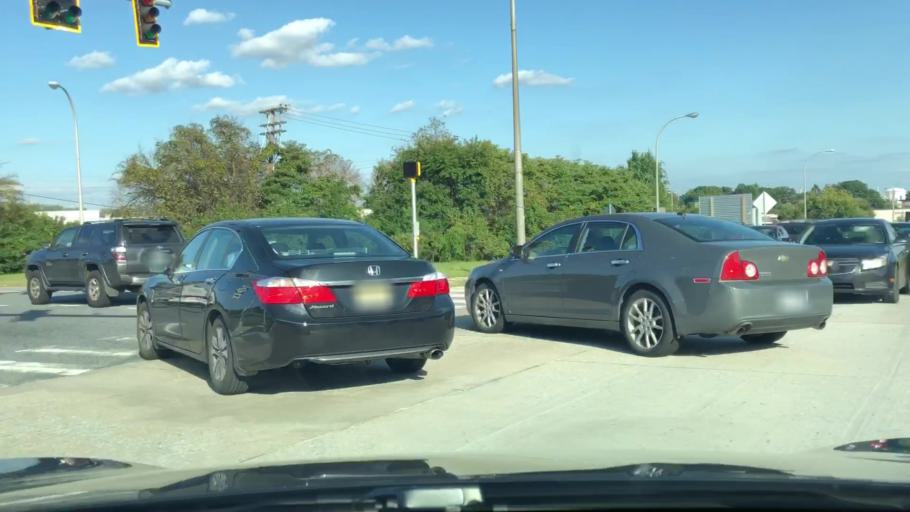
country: US
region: Delaware
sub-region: New Castle County
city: Claymont
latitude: 39.8153
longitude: -75.4523
